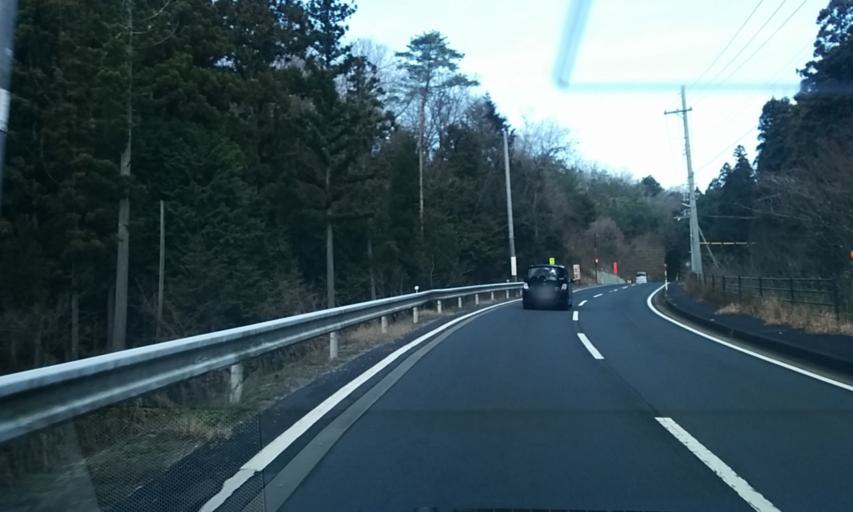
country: JP
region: Kyoto
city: Miyazu
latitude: 35.5802
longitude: 135.1184
